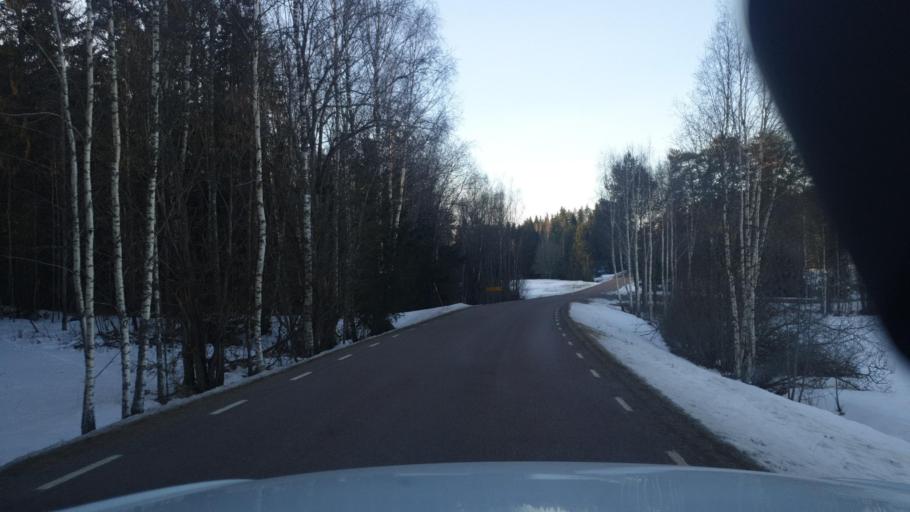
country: SE
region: Vaermland
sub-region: Karlstads Kommun
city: Edsvalla
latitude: 59.4964
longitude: 13.1056
